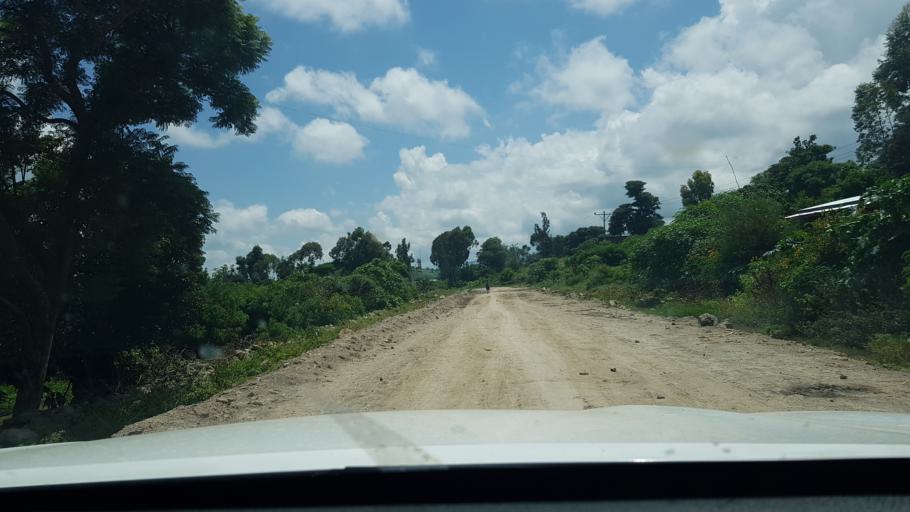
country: ET
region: Oromiya
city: Sirre
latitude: 8.4341
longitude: 39.8723
